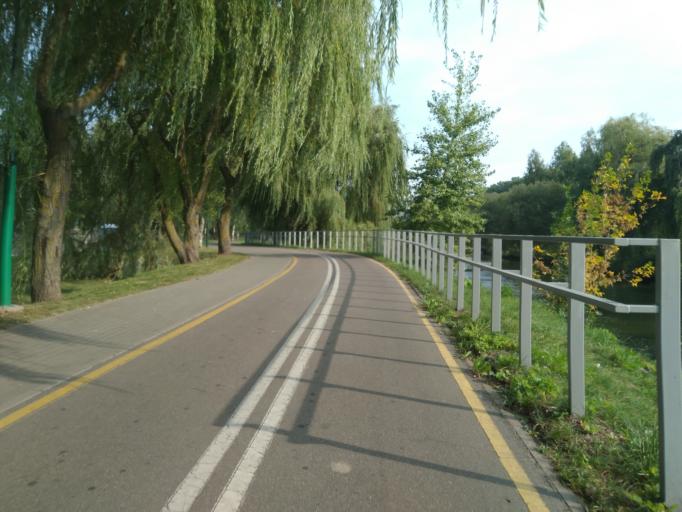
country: BY
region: Minsk
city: Minsk
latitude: 53.8708
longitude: 27.5861
